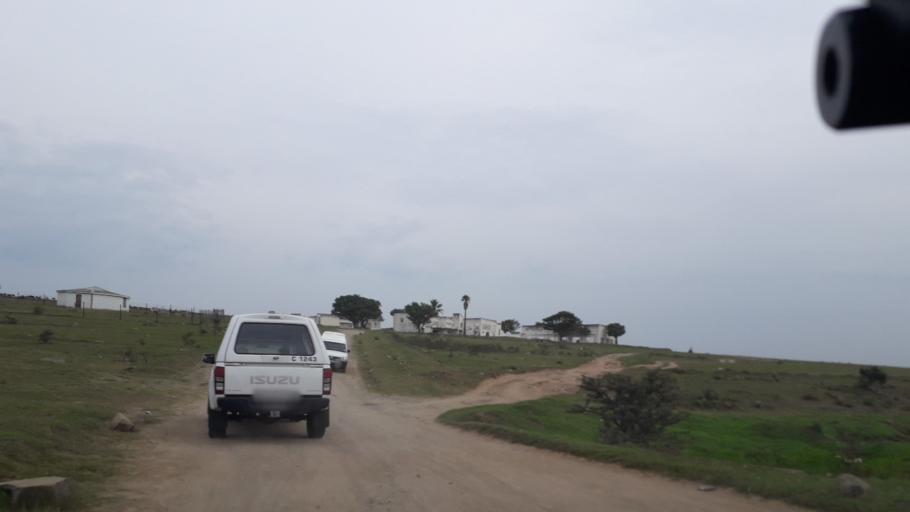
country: ZA
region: Eastern Cape
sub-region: Buffalo City Metropolitan Municipality
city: Bhisho
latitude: -32.8307
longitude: 27.3770
